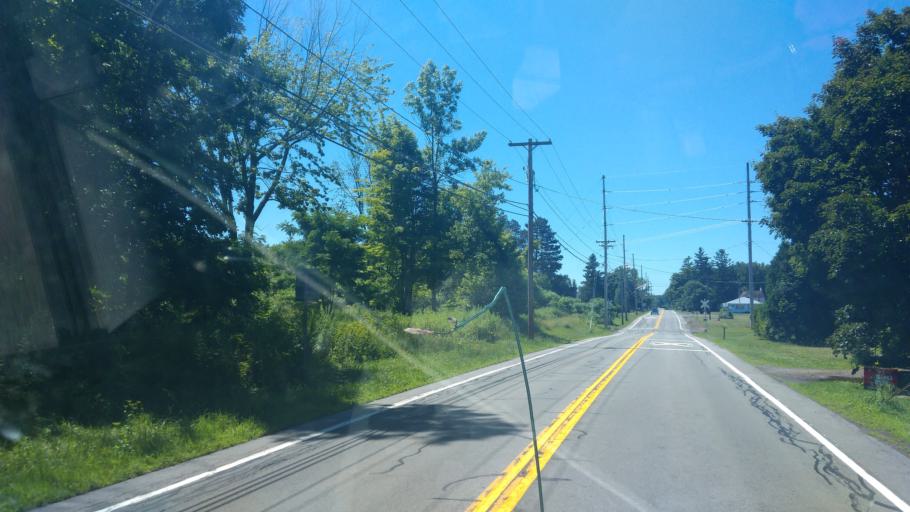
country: US
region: New York
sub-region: Wayne County
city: Sodus
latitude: 43.2041
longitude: -76.9830
